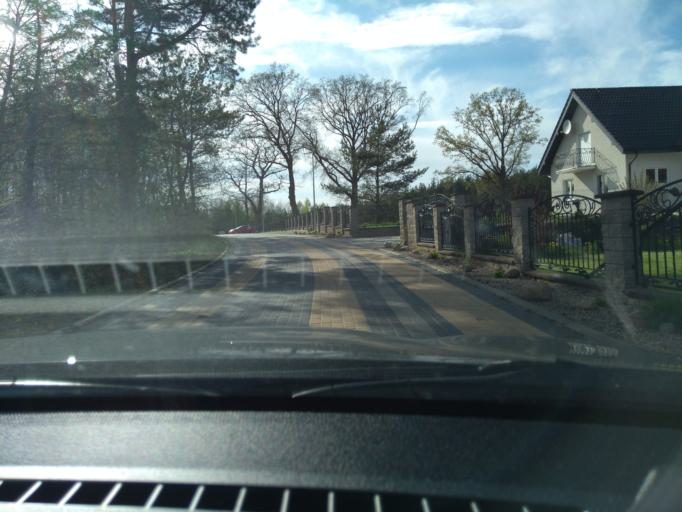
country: PL
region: Pomeranian Voivodeship
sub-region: Powiat leborski
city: Cewice
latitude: 54.3318
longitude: 17.6836
